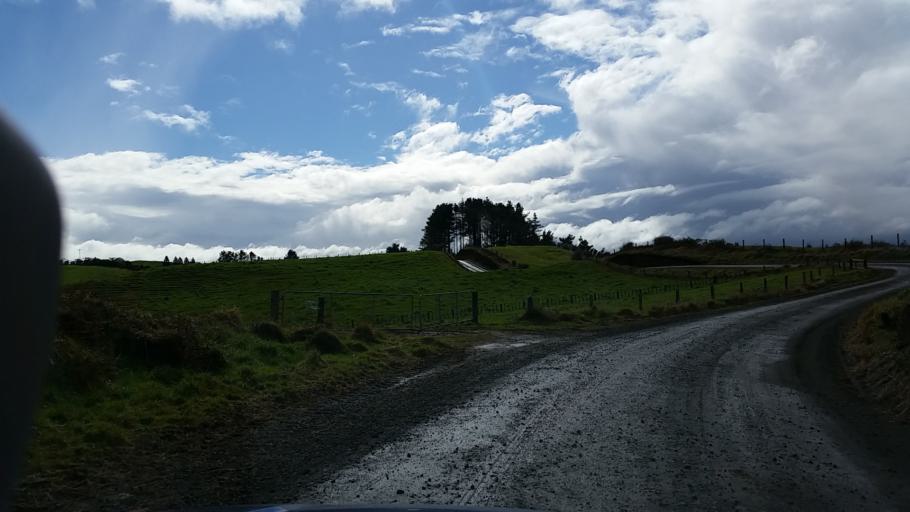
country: NZ
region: Taranaki
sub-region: South Taranaki District
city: Eltham
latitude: -39.2808
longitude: 174.3079
